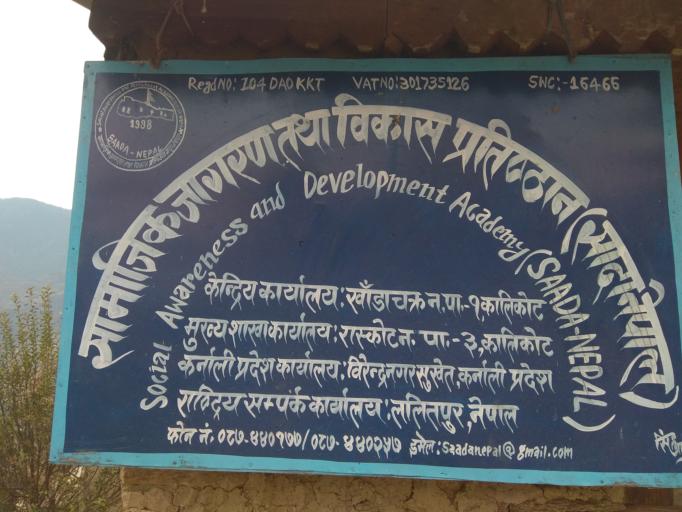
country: NP
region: Far Western
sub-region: Seti Zone
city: Achham
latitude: 29.2541
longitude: 81.6354
